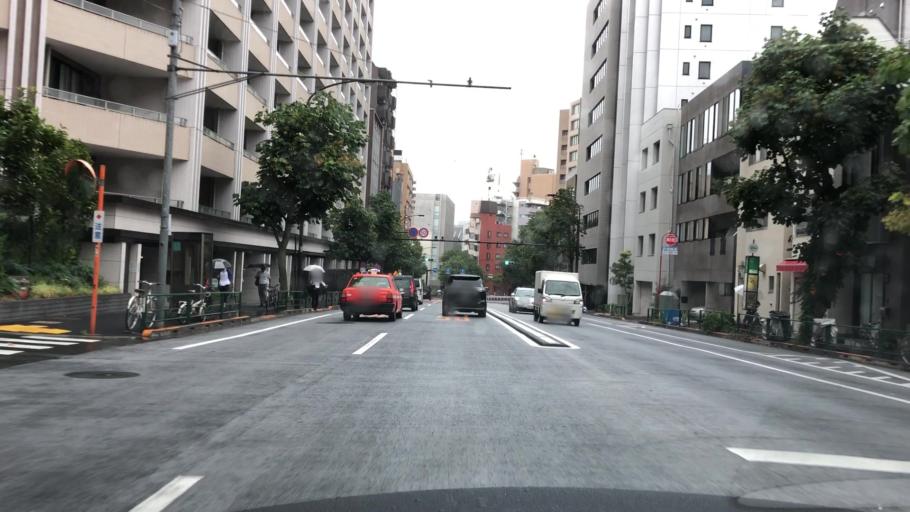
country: JP
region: Tokyo
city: Tokyo
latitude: 35.6845
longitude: 139.7159
